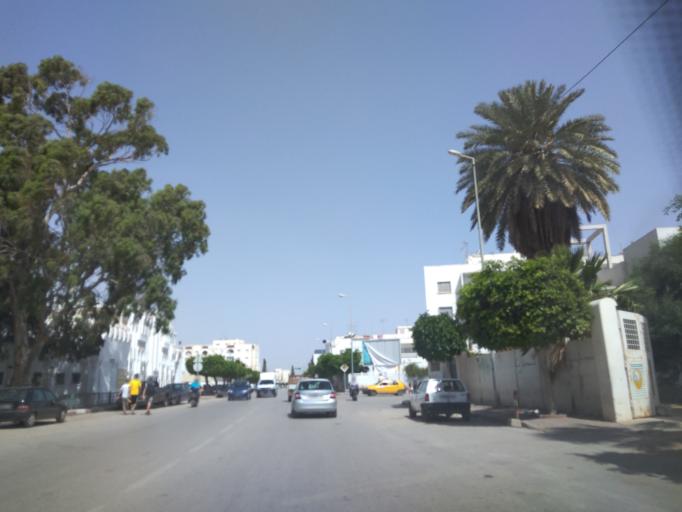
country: TN
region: Safaqis
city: Sfax
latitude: 34.7417
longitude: 10.7515
